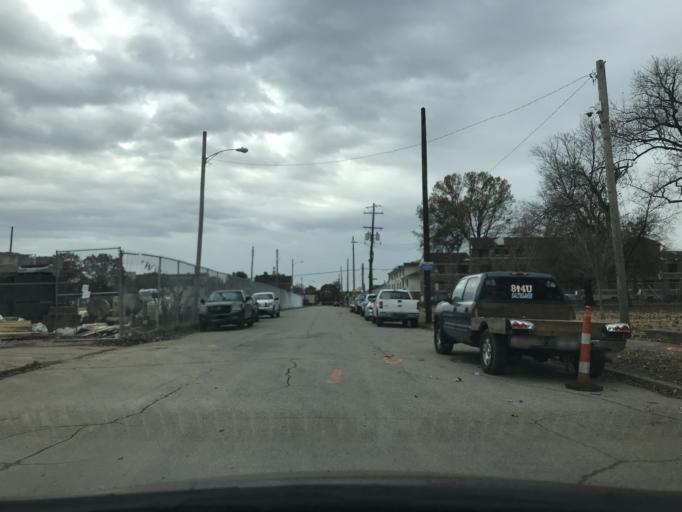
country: US
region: Kentucky
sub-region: Jefferson County
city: Louisville
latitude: 38.2545
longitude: -85.7687
